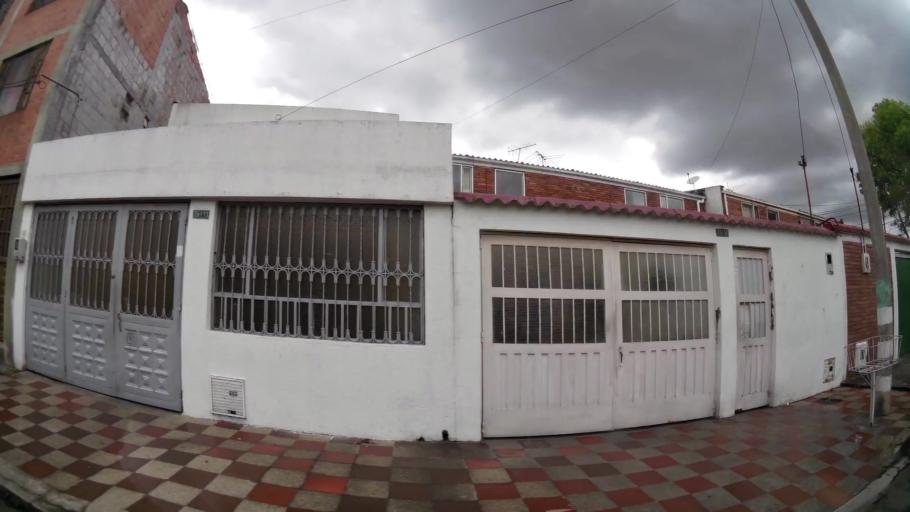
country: CO
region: Bogota D.C.
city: Barrio San Luis
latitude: 4.7091
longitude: -74.0913
